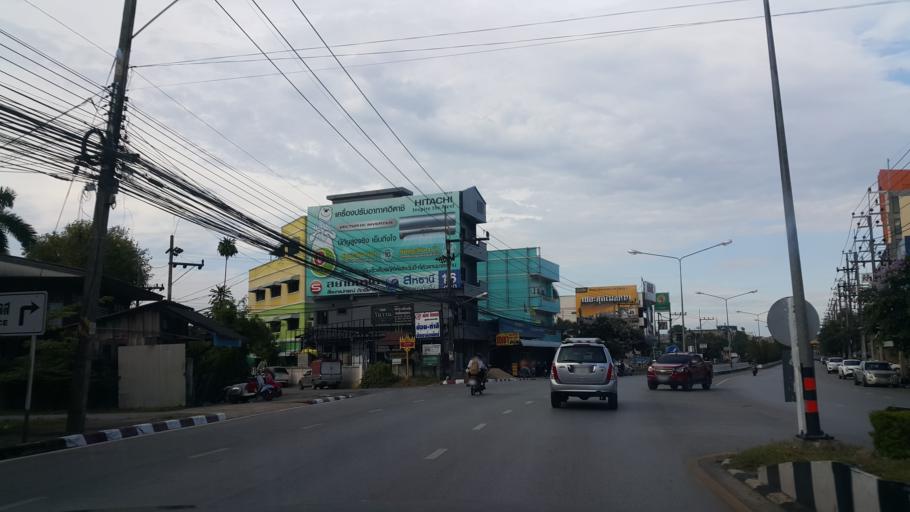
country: TH
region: Chiang Rai
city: Chiang Rai
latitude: 19.9132
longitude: 99.8424
